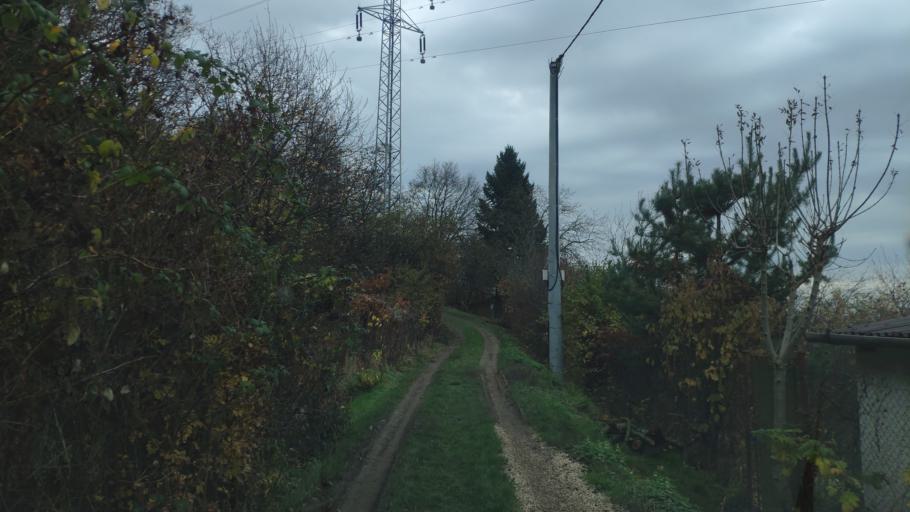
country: SK
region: Kosicky
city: Kosice
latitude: 48.6965
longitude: 21.2914
